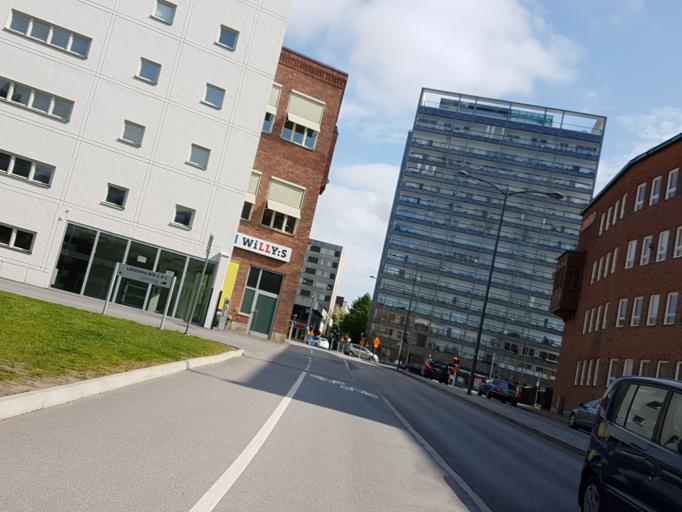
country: SE
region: Stockholm
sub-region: Sundbybergs Kommun
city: Sundbyberg
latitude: 59.3618
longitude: 17.9624
